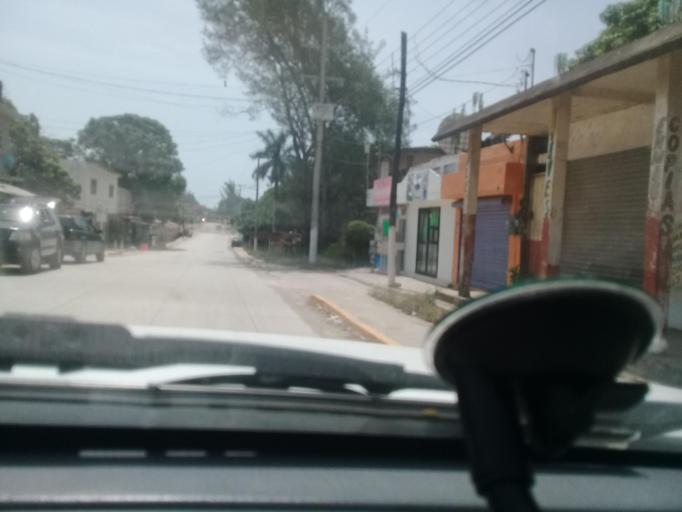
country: MX
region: Veracruz
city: Anahuac
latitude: 22.2291
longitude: -97.8292
